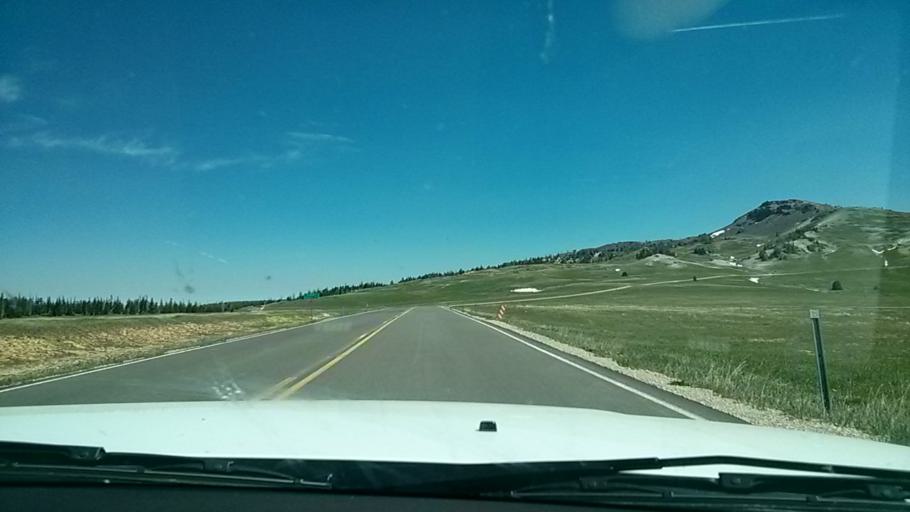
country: US
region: Utah
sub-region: Iron County
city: Parowan
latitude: 37.6639
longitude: -112.8379
